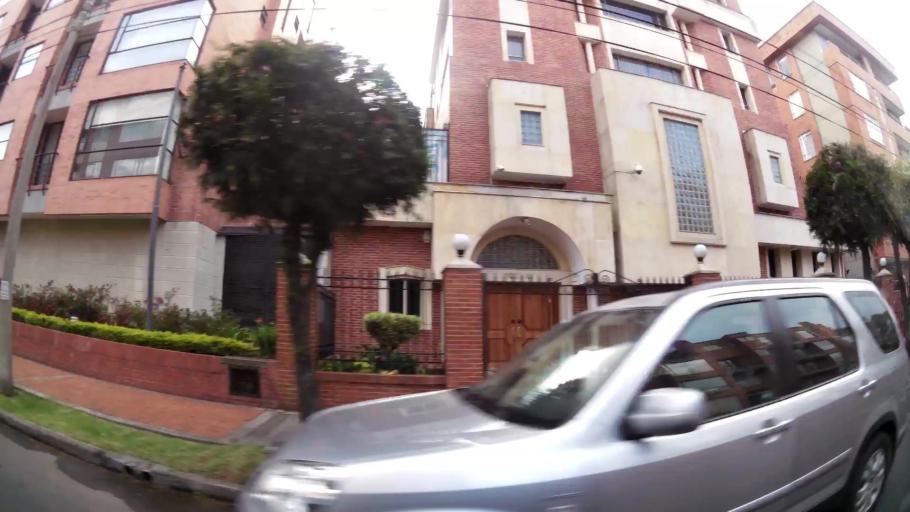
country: CO
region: Bogota D.C.
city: Barrio San Luis
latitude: 4.6898
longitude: -74.0555
